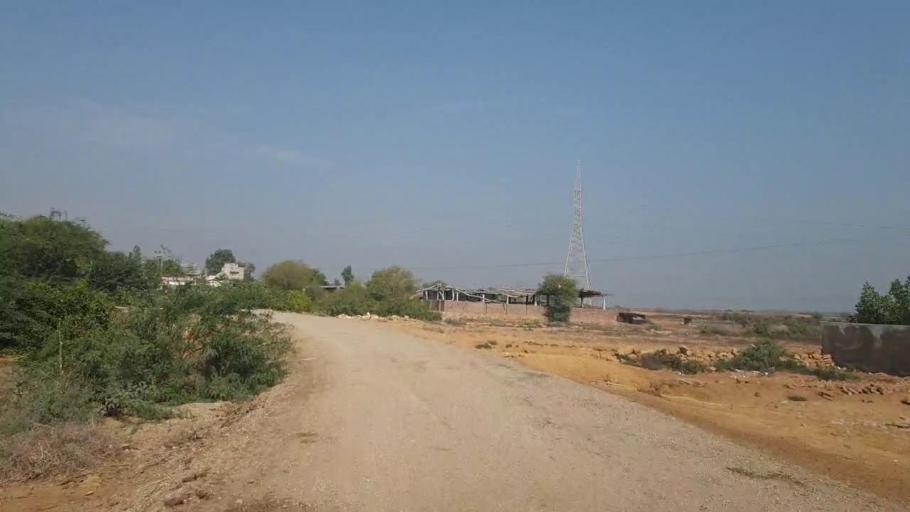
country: PK
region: Sindh
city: Jamshoro
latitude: 25.4618
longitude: 68.2926
